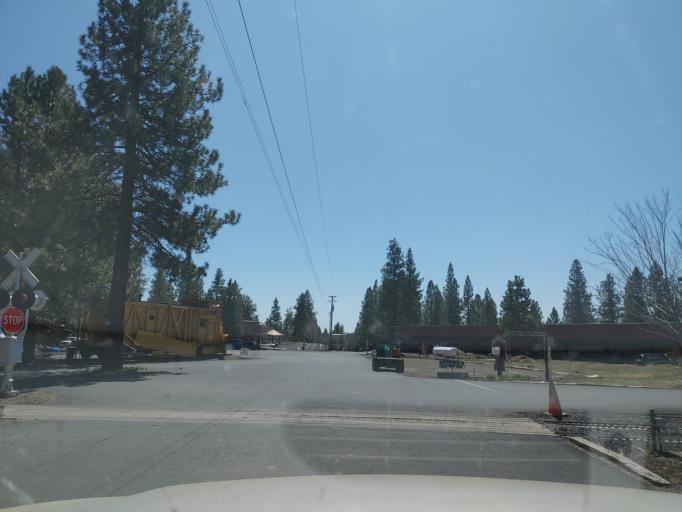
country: US
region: Oregon
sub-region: Klamath County
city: Klamath Falls
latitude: 42.5580
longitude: -121.8869
